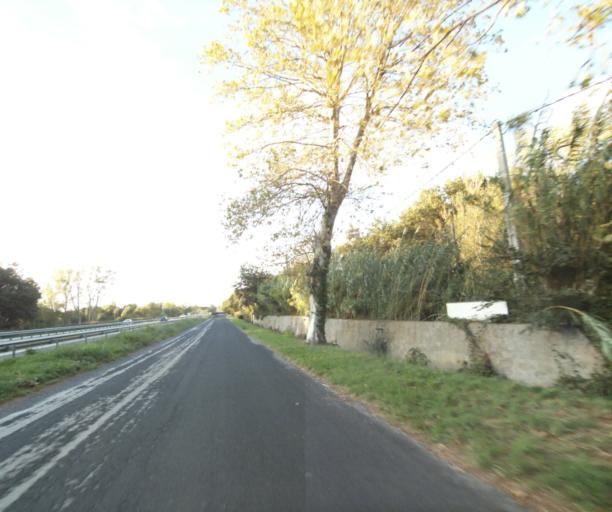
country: FR
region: Languedoc-Roussillon
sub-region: Departement des Pyrenees-Orientales
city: Argelers
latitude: 42.5697
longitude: 3.0001
